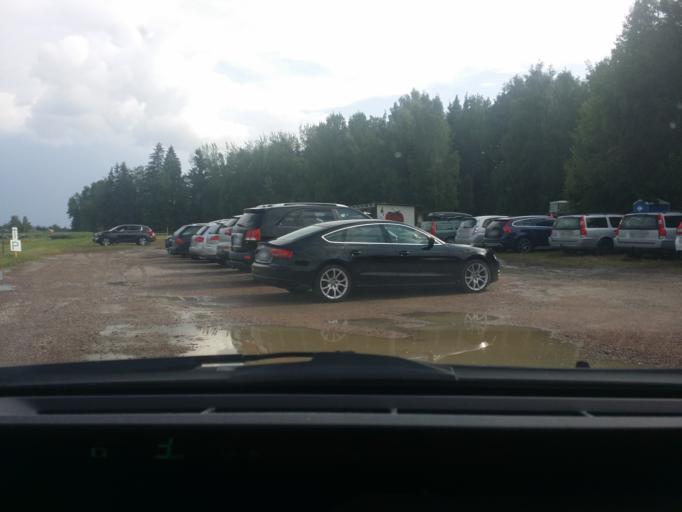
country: SE
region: Vaestmanland
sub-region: Hallstahammars Kommun
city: Kolback
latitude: 59.5652
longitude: 16.2158
